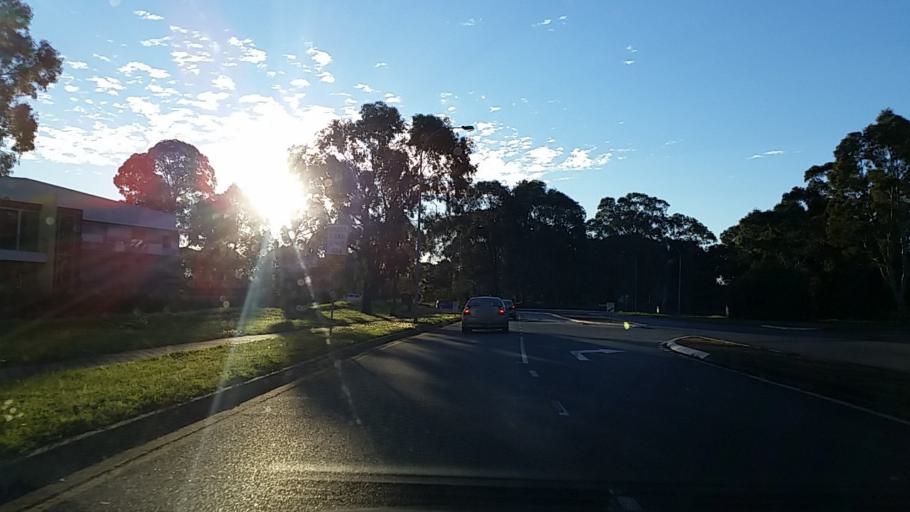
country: AU
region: South Australia
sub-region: Salisbury
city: Salisbury
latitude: -34.7483
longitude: 138.6399
